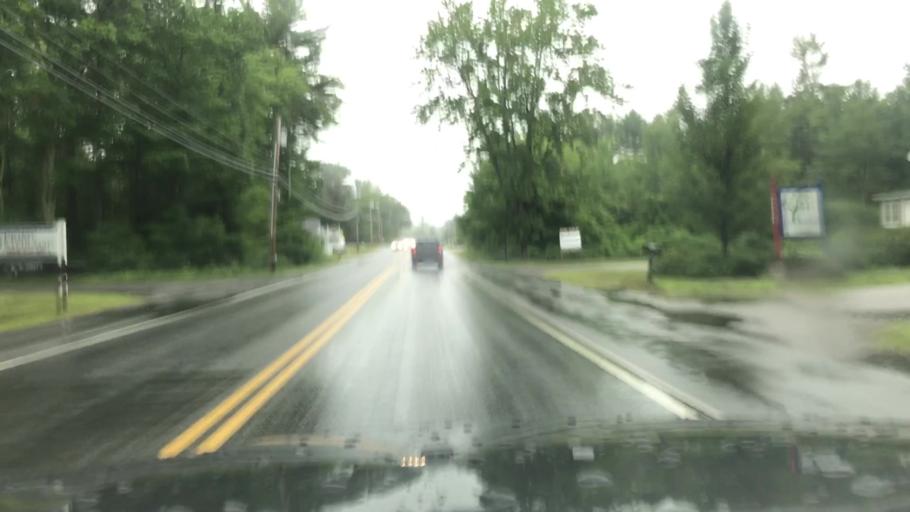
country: US
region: Maine
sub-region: York County
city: Kennebunk
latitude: 43.4167
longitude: -70.5183
